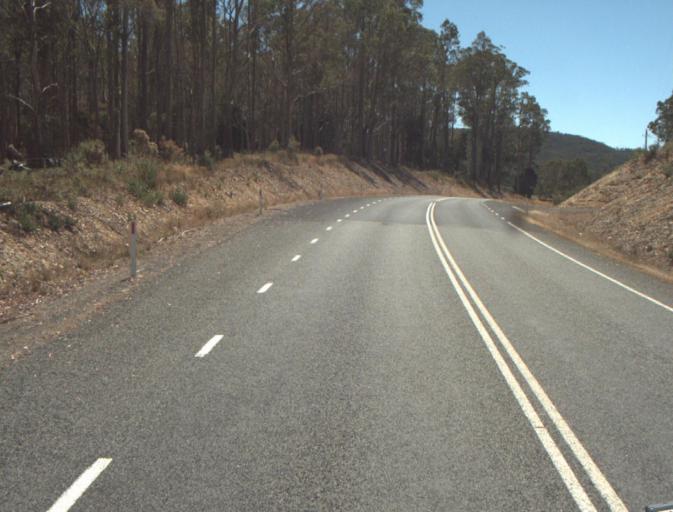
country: AU
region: Tasmania
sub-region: Launceston
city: Newstead
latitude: -41.3370
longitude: 147.3474
